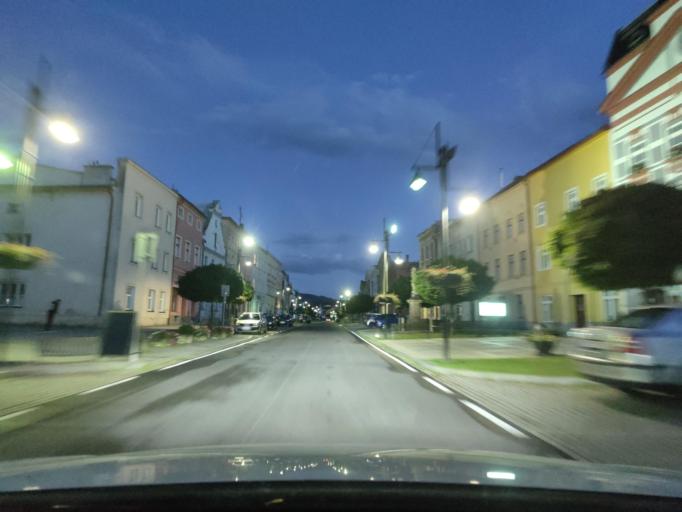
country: CZ
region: Olomoucky
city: Zlate Hory
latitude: 50.2643
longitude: 17.3959
